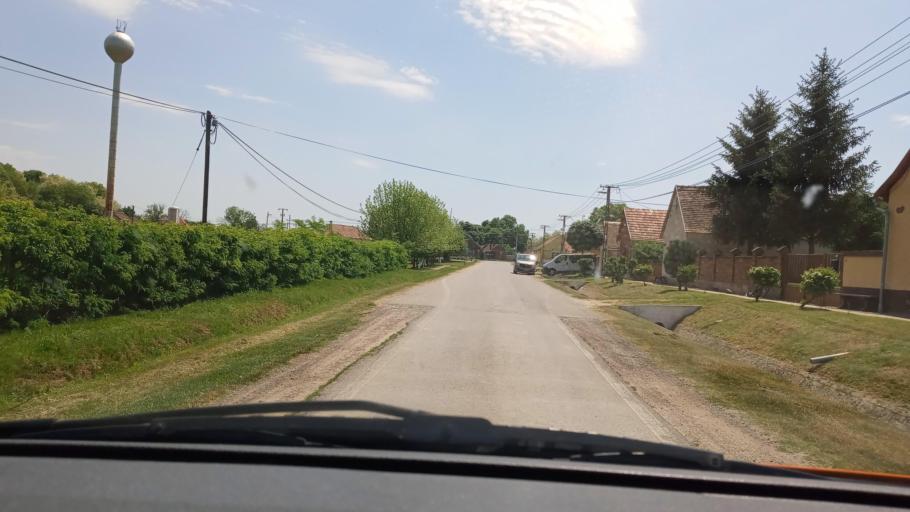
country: HU
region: Baranya
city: Harkany
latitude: 45.8305
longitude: 18.1377
